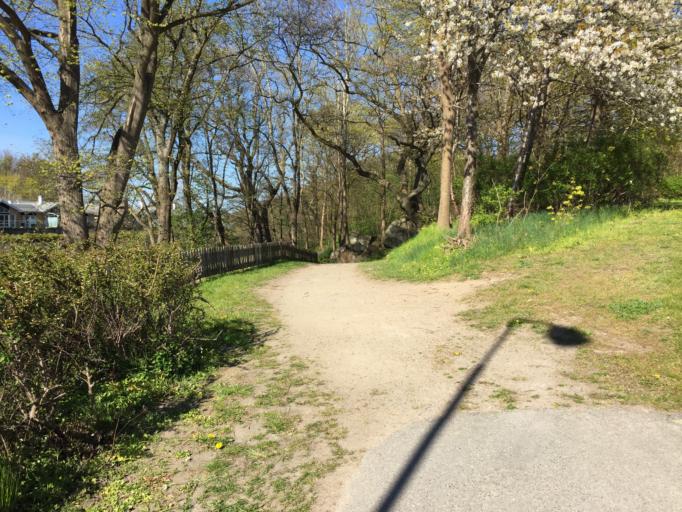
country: SE
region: Blekinge
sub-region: Karlskrona Kommun
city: Rodeby
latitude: 56.1969
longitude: 15.6609
